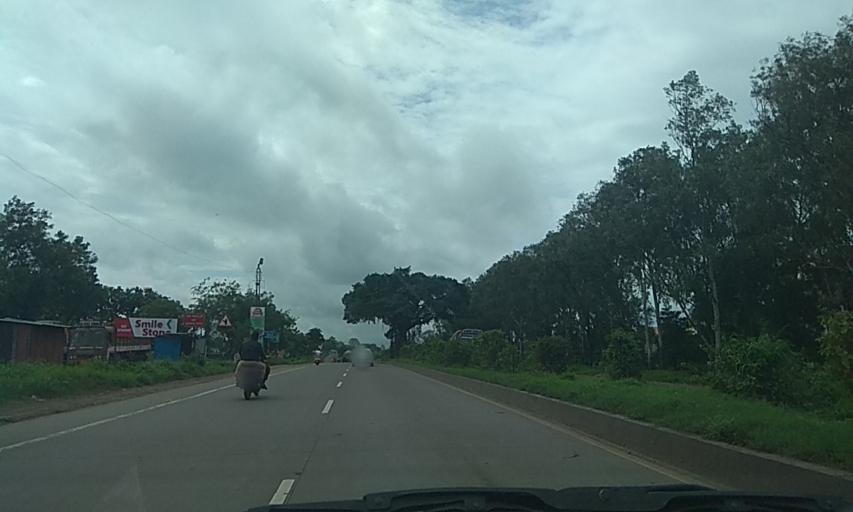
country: IN
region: Maharashtra
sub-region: Kolhapur
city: Kagal
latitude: 16.6360
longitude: 74.2839
